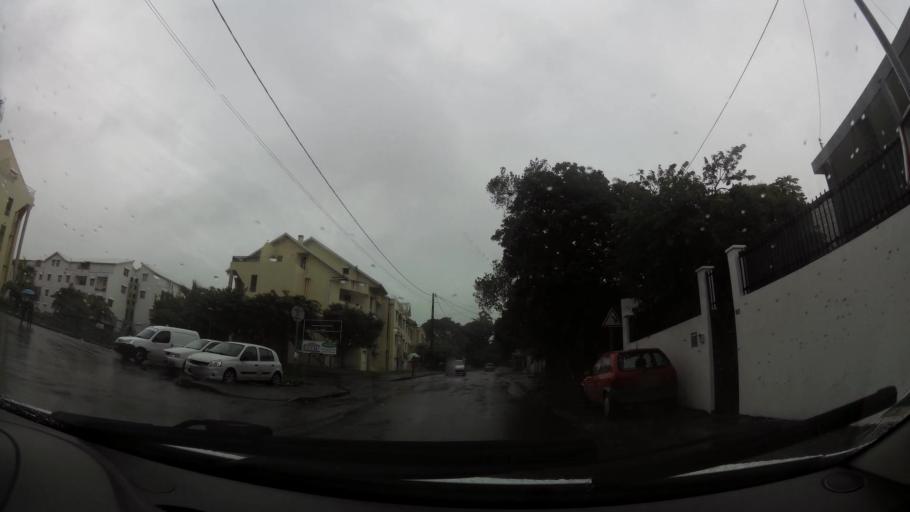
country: RE
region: Reunion
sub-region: Reunion
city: Saint-Andre
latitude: -20.9623
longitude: 55.6475
